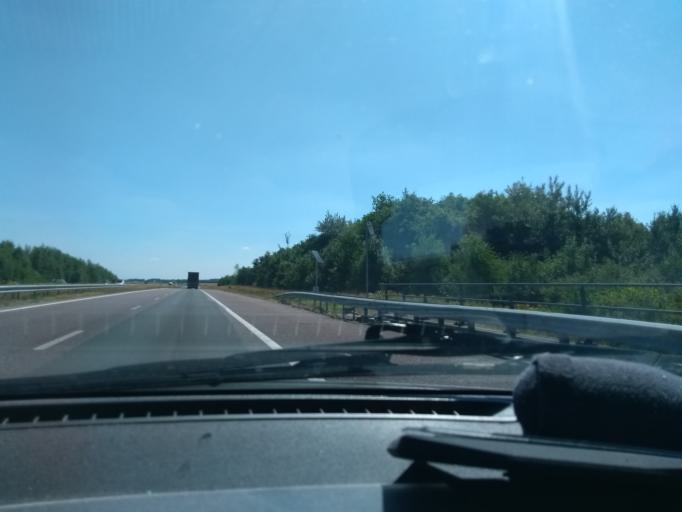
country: NL
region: Drenthe
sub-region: Gemeente Emmen
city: Schoonebeek
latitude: 52.7229
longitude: 6.8777
